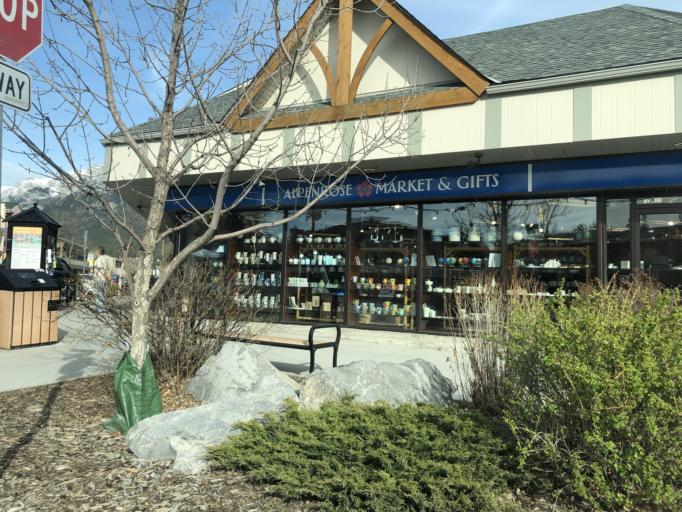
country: CA
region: Alberta
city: Canmore
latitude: 51.0891
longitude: -115.3632
